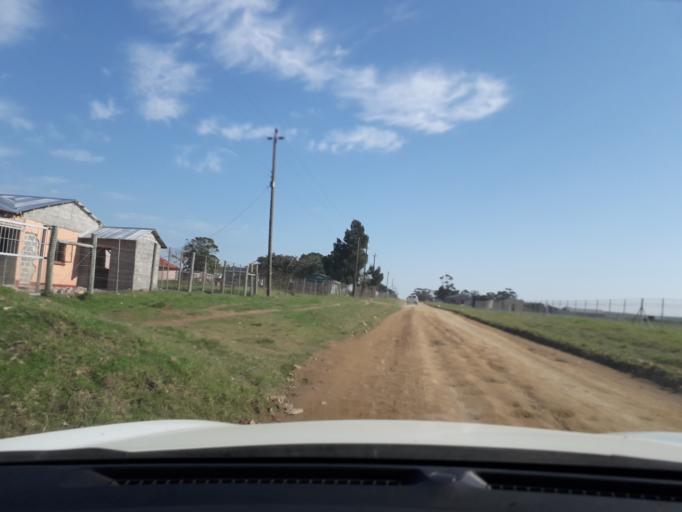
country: ZA
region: Eastern Cape
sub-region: Buffalo City Metropolitan Municipality
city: Bhisho
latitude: -32.9717
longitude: 27.3090
